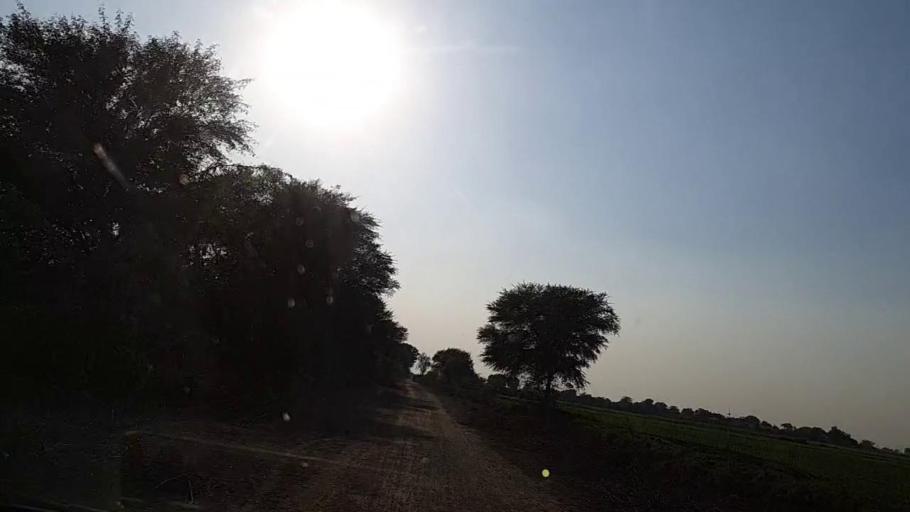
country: PK
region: Sindh
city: Sakrand
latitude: 26.0942
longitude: 68.2143
